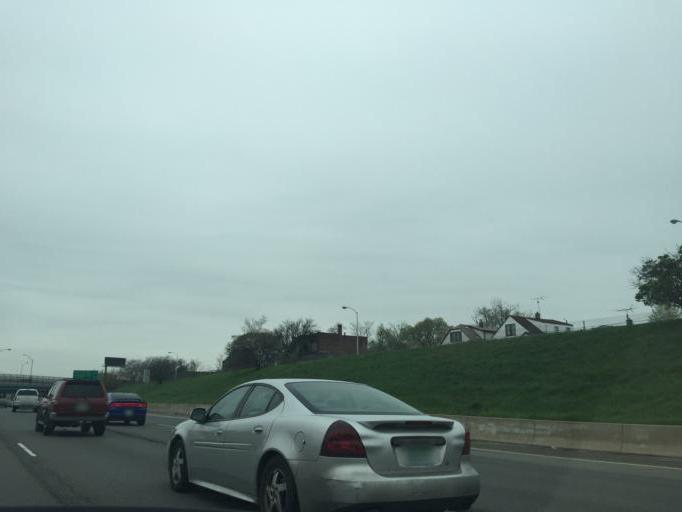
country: US
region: Michigan
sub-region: Wayne County
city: Highland Park
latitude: 42.3794
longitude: -83.1463
